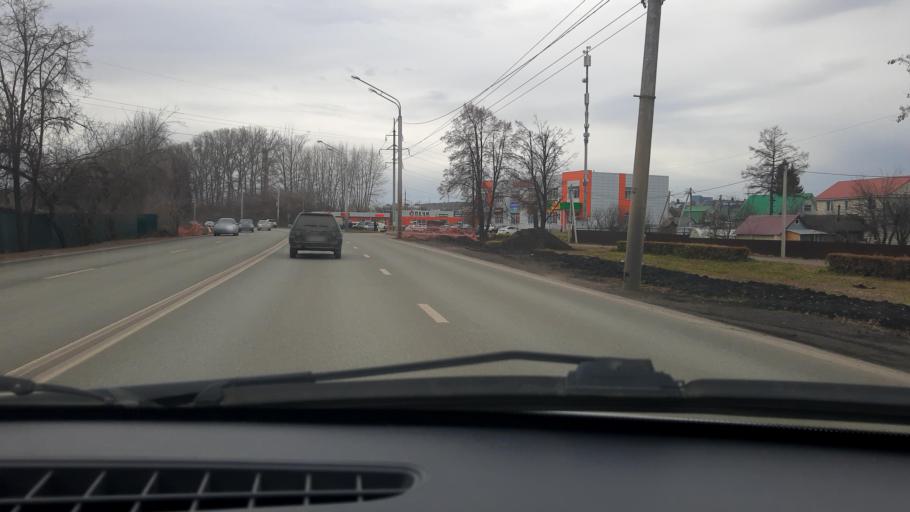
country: RU
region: Bashkortostan
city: Avdon
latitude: 54.6921
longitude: 55.8204
